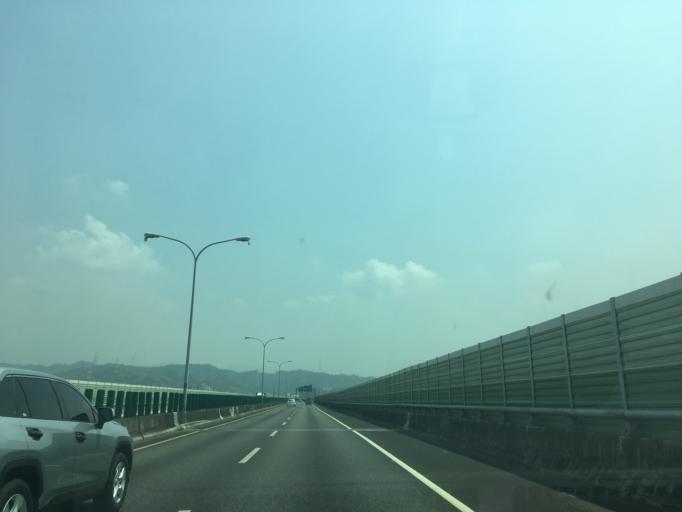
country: TW
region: Taiwan
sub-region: Taichung City
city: Taichung
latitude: 24.0749
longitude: 120.6853
